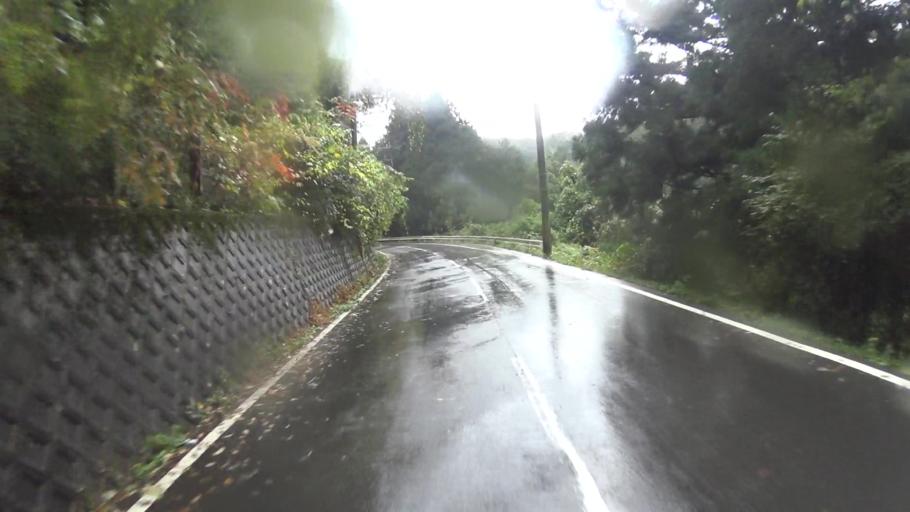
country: JP
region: Kyoto
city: Miyazu
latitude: 35.4362
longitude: 135.1584
